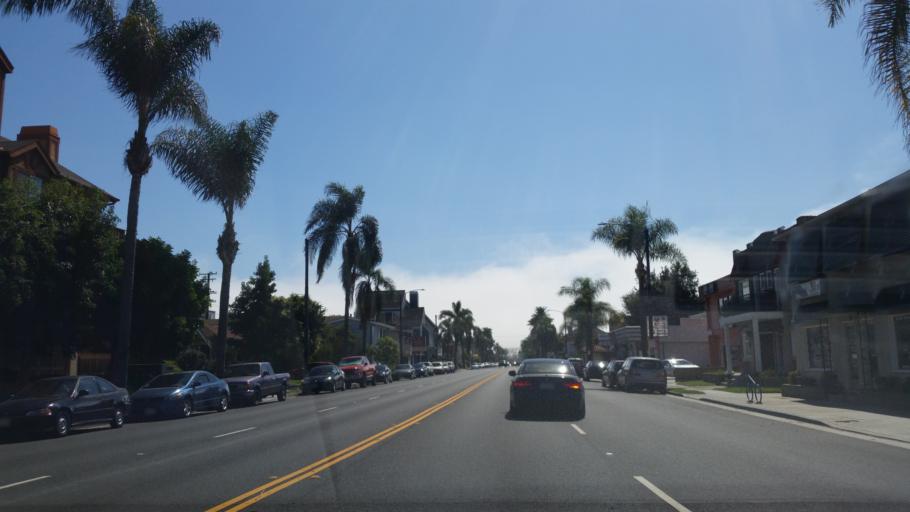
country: US
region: California
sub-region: Los Angeles County
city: Signal Hill
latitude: 33.7713
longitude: -118.1525
